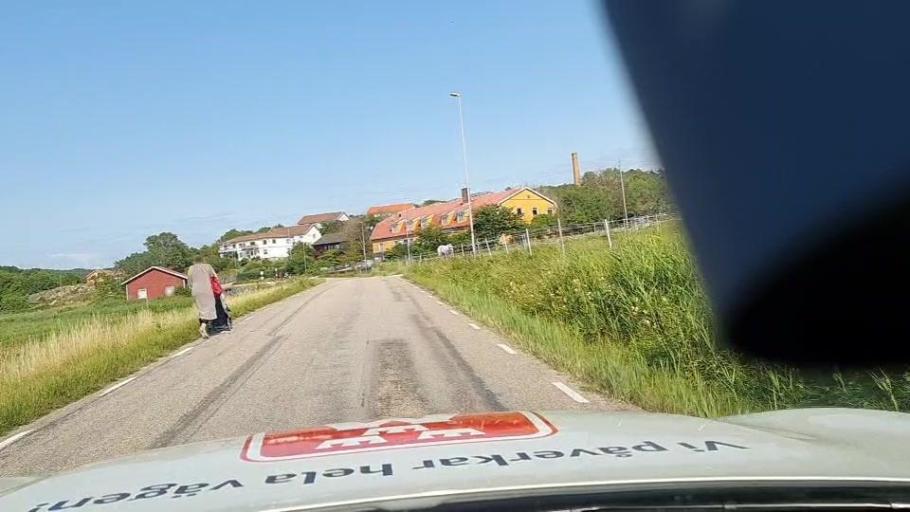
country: SE
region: Vaestra Goetaland
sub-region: Lysekils Kommun
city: Lysekil
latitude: 58.1273
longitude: 11.4469
